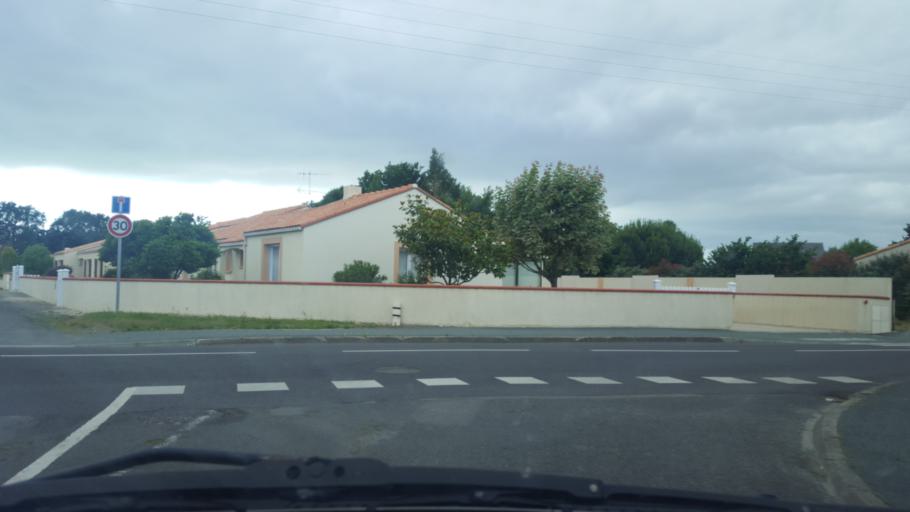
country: FR
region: Pays de la Loire
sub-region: Departement de la Loire-Atlantique
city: Saint-Philbert-de-Grand-Lieu
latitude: 47.0335
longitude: -1.6444
